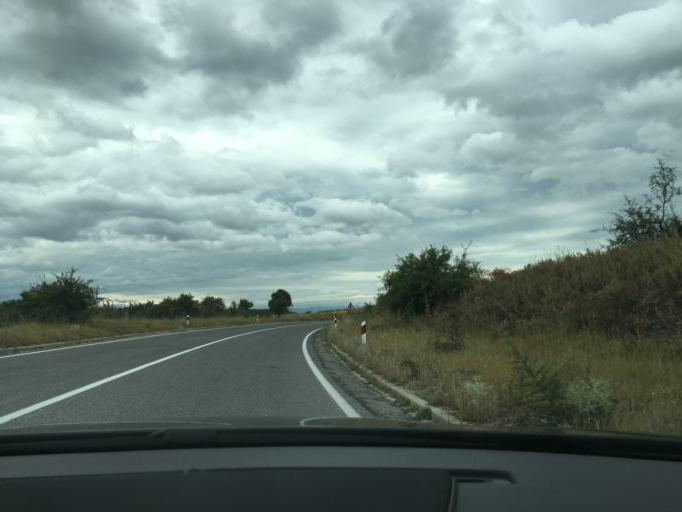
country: MK
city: Klechovce
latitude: 42.1475
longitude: 21.9796
